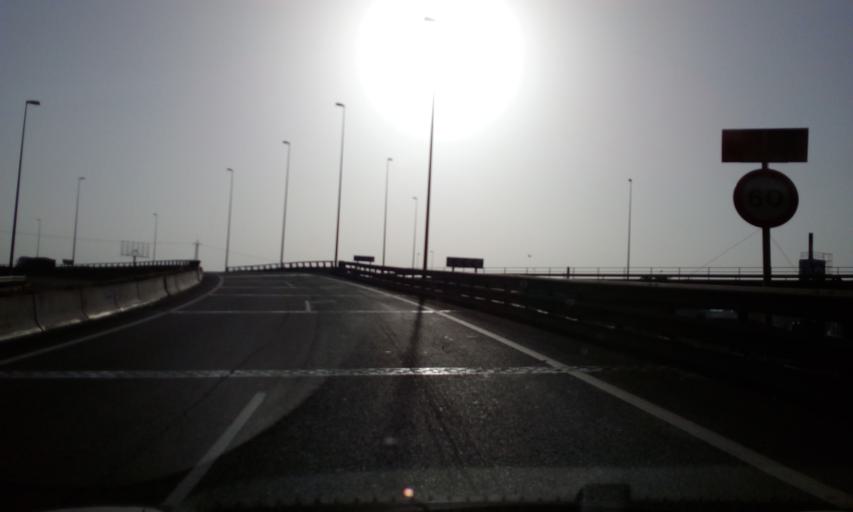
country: ES
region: Andalusia
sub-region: Provincia de Sevilla
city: San Juan de Aznalfarache
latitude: 37.3721
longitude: -6.0274
